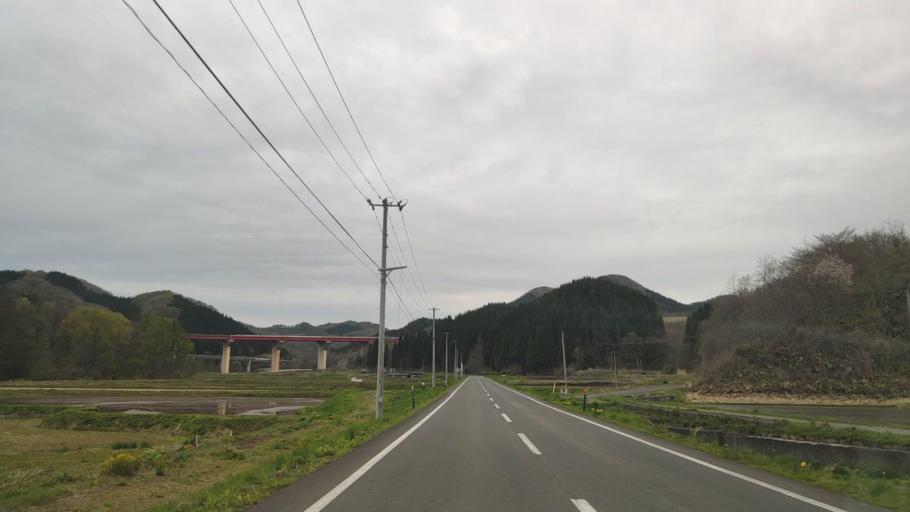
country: JP
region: Akita
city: Odate
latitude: 40.3714
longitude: 140.7237
